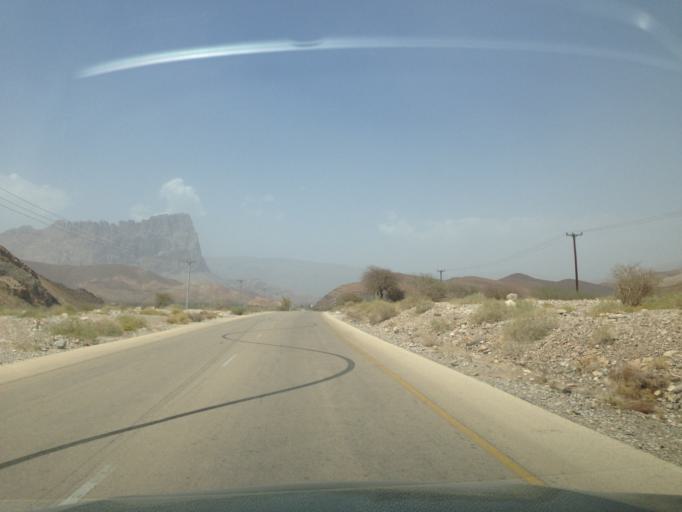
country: OM
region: Az Zahirah
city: `Ibri
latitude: 23.1932
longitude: 56.9290
